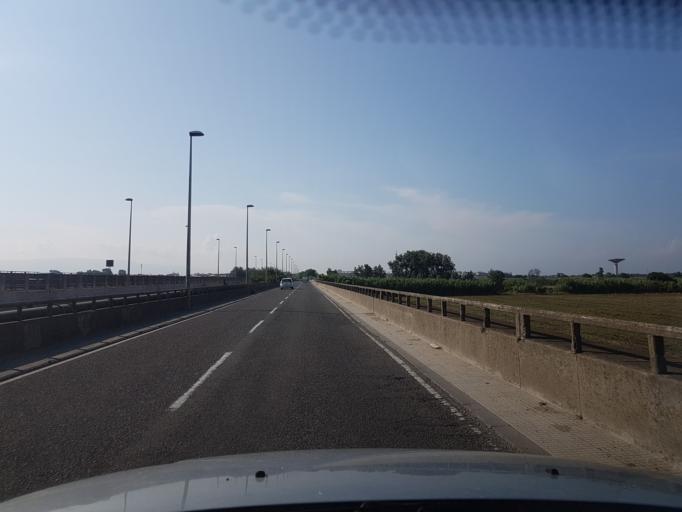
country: IT
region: Sardinia
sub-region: Provincia di Oristano
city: Donigala Fenugheddu
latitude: 39.9208
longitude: 8.5821
